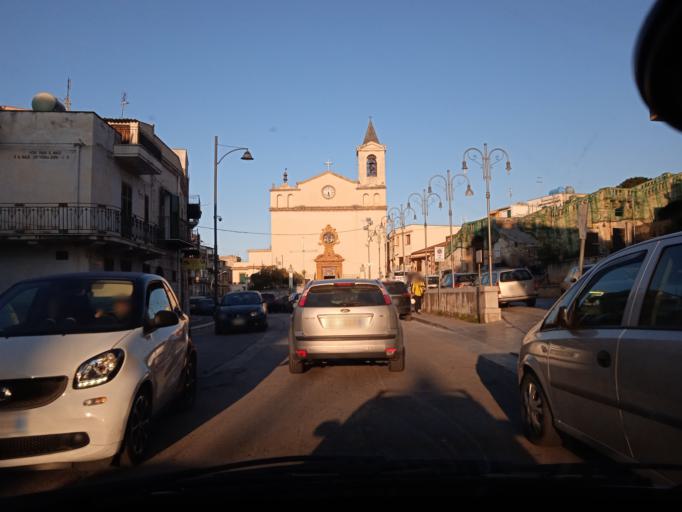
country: IT
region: Sicily
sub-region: Palermo
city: Ficarazzi
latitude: 38.0893
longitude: 13.4696
